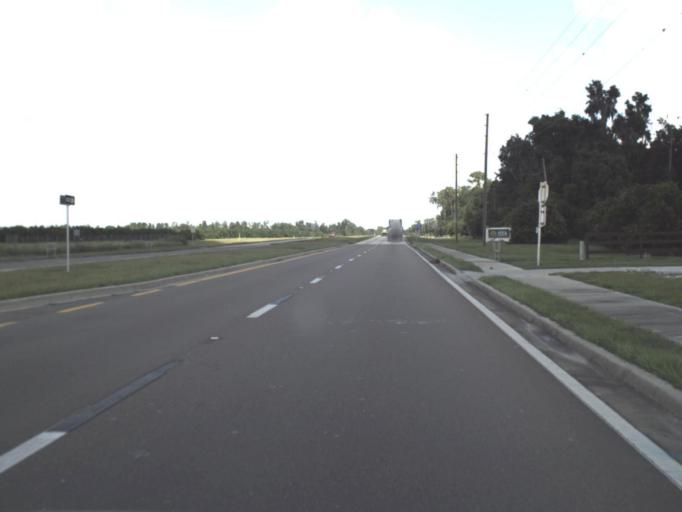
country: US
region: Florida
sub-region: Hardee County
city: Bowling Green
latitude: 27.6486
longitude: -81.8226
